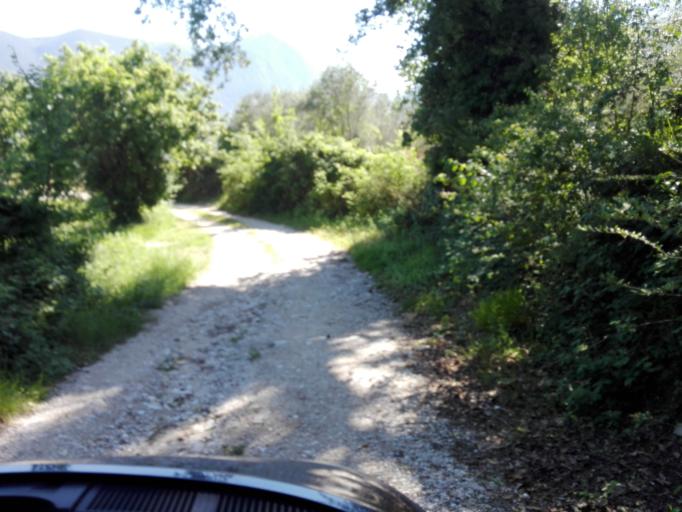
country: IT
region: Umbria
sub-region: Provincia di Perugia
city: Foligno
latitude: 42.9777
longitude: 12.7430
